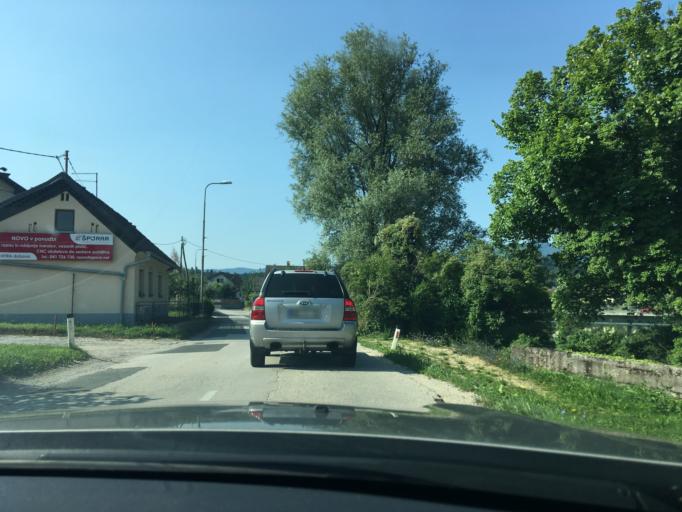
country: SI
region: Straza
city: Straza
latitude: 45.7820
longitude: 15.0768
